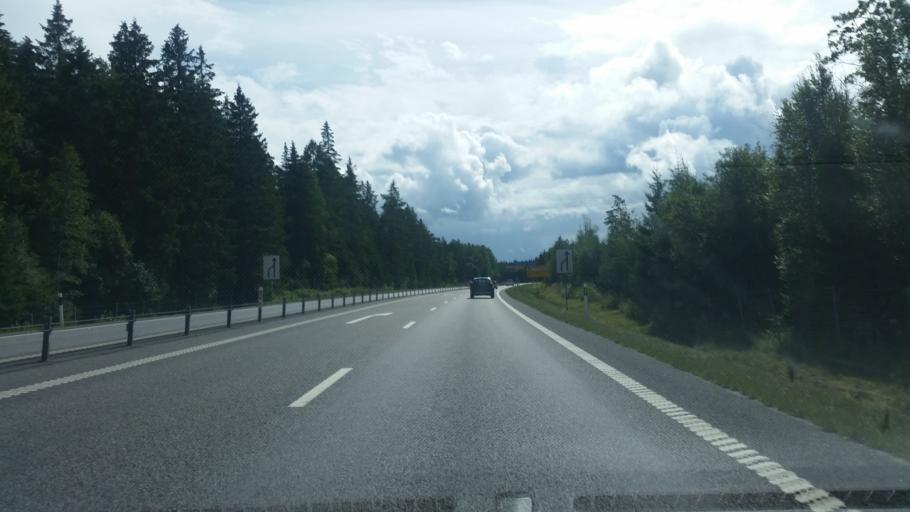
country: SE
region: Joenkoeping
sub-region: Mullsjo Kommun
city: Mullsjoe
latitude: 57.7695
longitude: 13.7179
